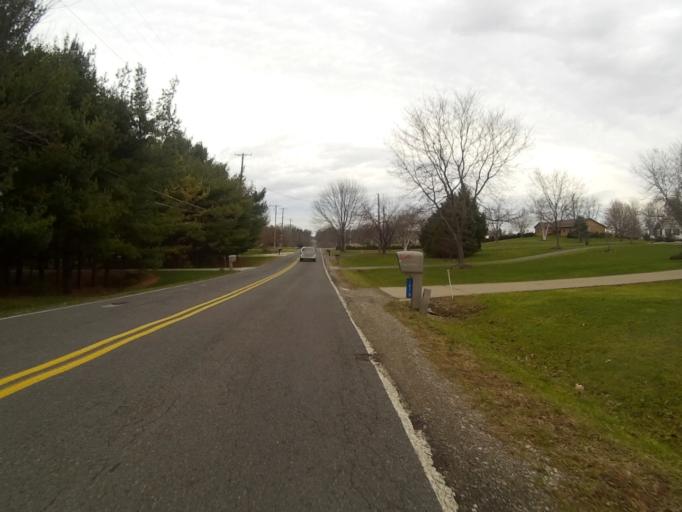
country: US
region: Ohio
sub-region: Stark County
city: Hartville
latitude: 41.0181
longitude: -81.3293
